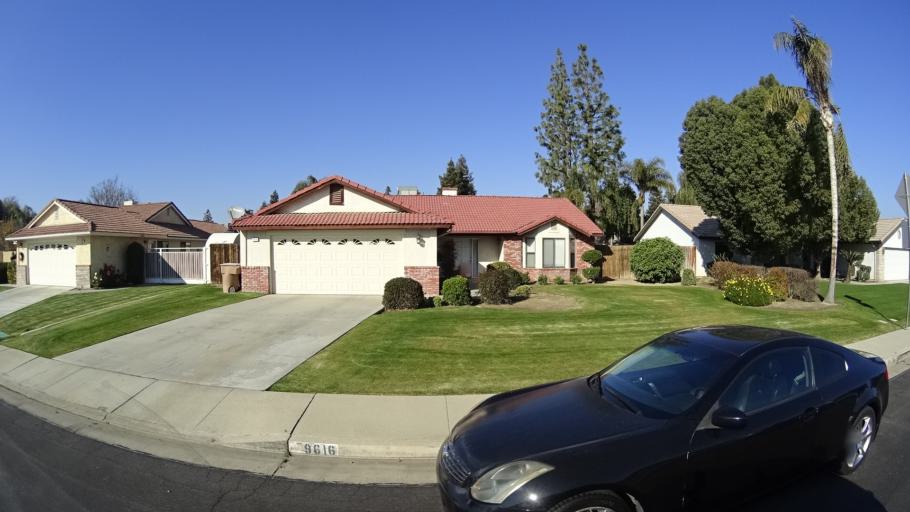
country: US
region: California
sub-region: Kern County
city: Greenacres
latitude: 35.3276
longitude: -119.1084
